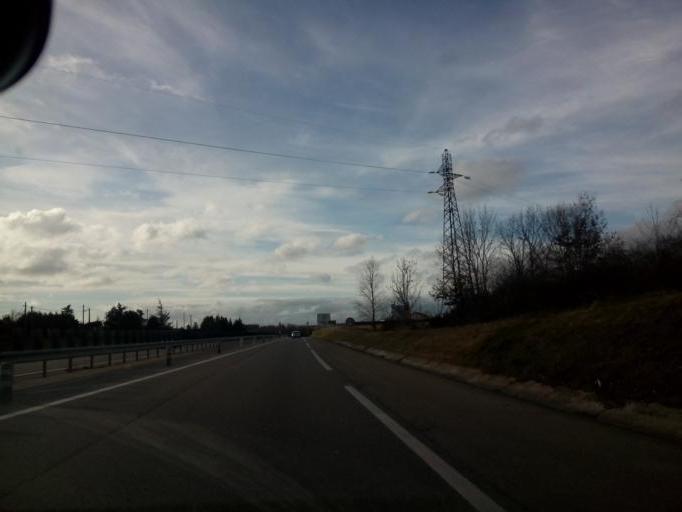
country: FR
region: Rhone-Alpes
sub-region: Departement de l'Ardeche
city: Peaugres
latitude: 45.2948
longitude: 4.7365
